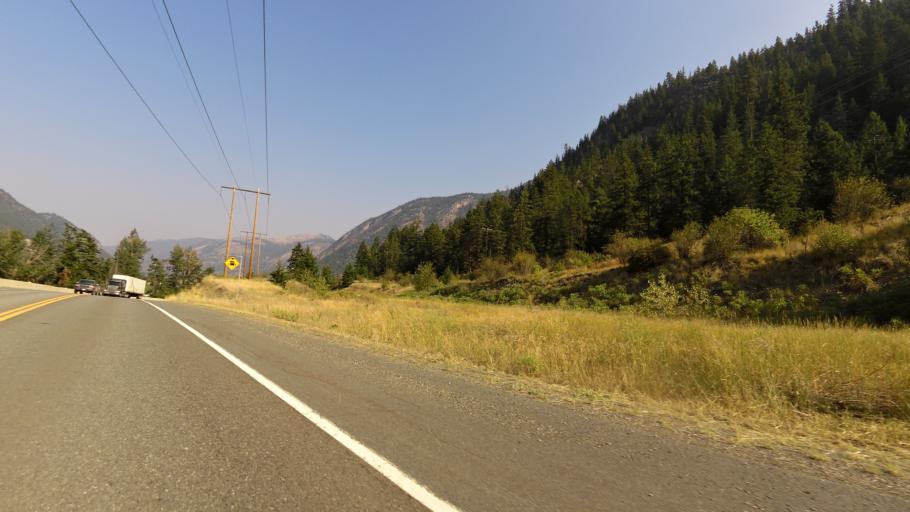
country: CA
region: British Columbia
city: Summerland
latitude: 49.3252
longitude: -120.0438
